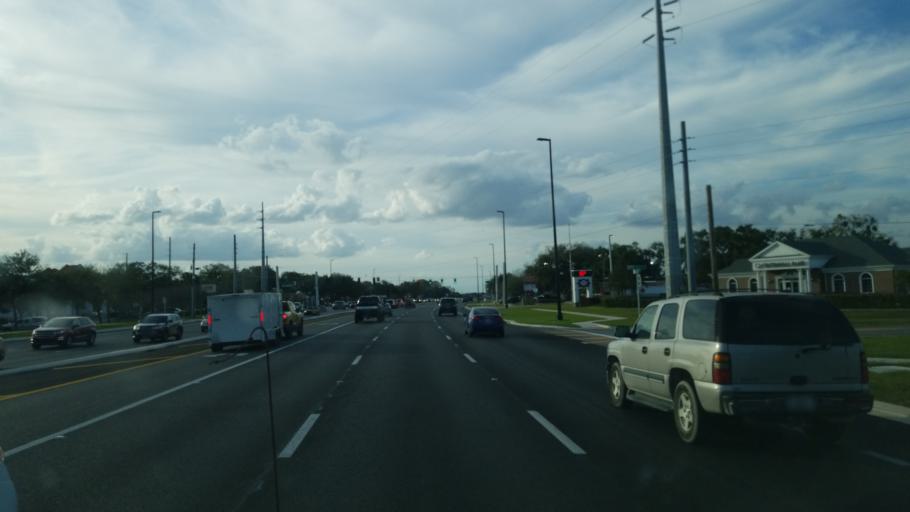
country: US
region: Florida
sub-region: Osceola County
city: Saint Cloud
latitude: 28.2482
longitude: -81.3082
